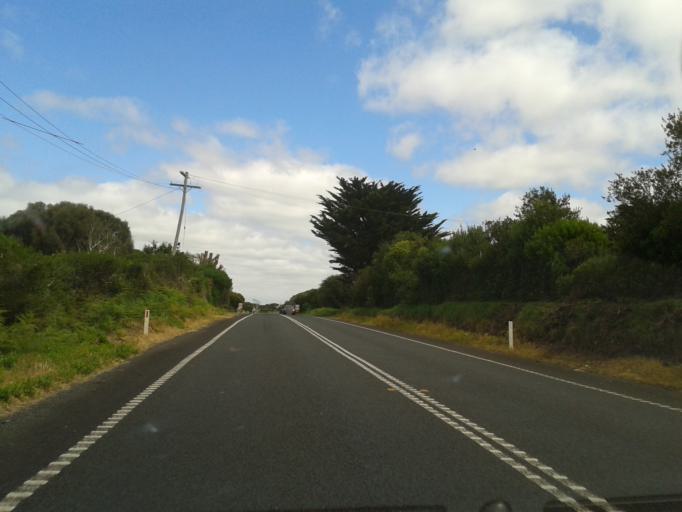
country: AU
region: Victoria
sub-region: Glenelg
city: Portland
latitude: -38.2511
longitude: 141.7242
